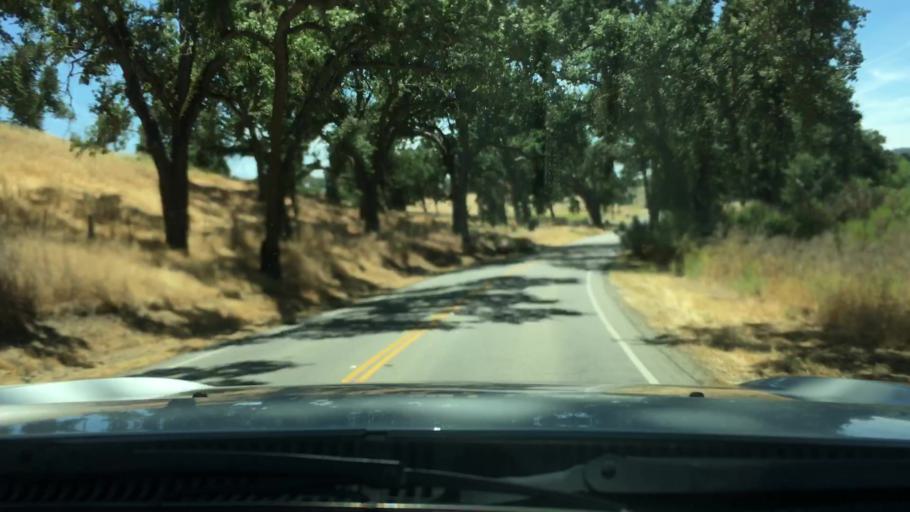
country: US
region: California
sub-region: San Luis Obispo County
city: Templeton
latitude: 35.5562
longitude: -120.6899
